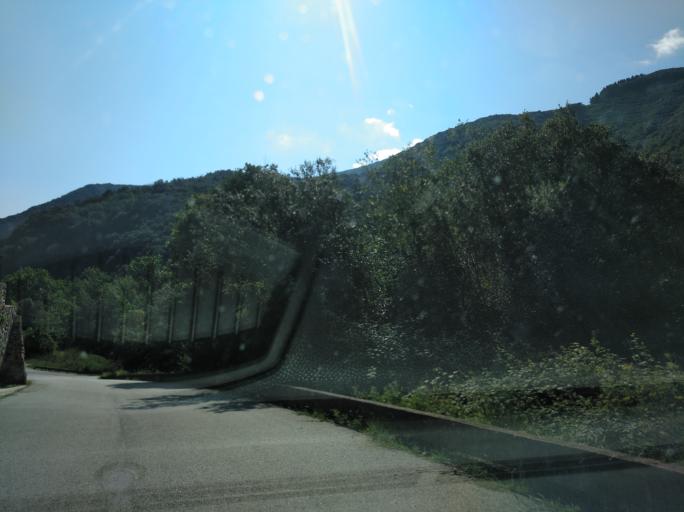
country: ES
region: Catalonia
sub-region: Provincia de Girona
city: Susqueda
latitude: 41.9840
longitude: 2.5407
